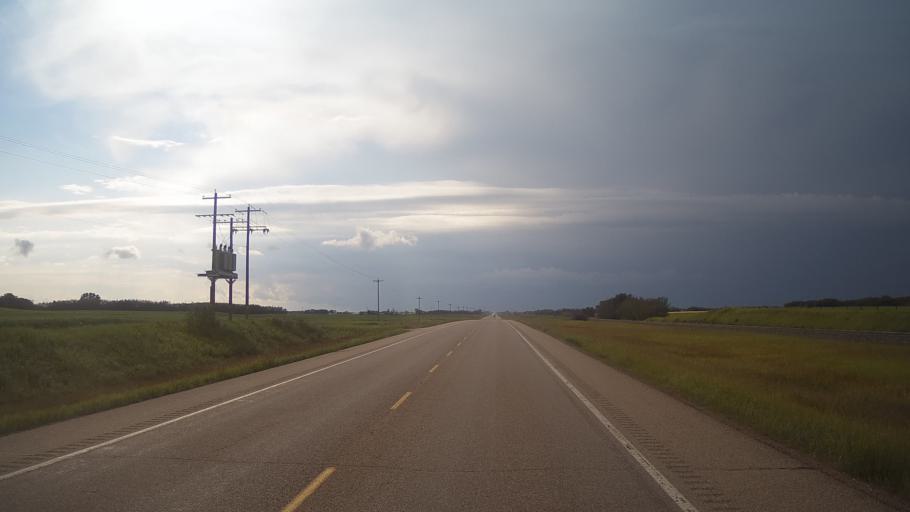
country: CA
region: Alberta
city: Viking
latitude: 53.1790
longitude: -112.0654
